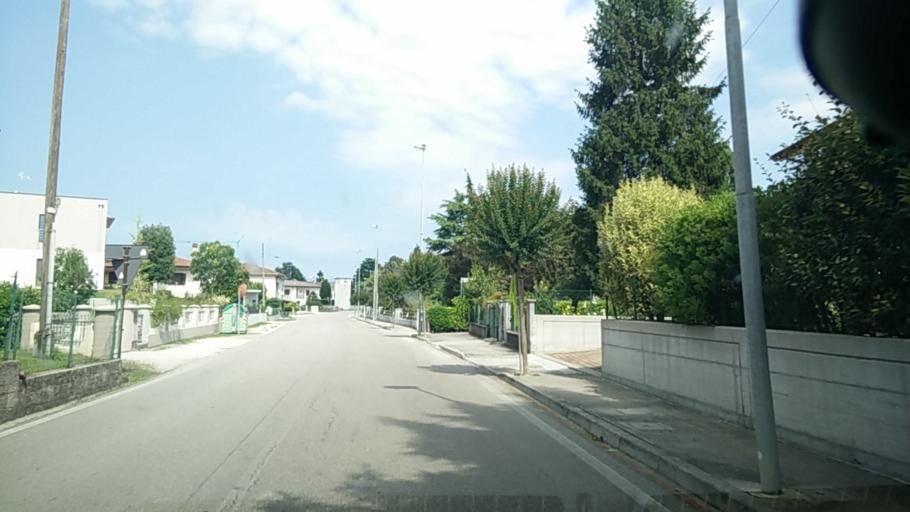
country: IT
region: Friuli Venezia Giulia
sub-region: Provincia di Pordenone
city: Puia-Villanova
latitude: 45.8445
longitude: 12.5646
